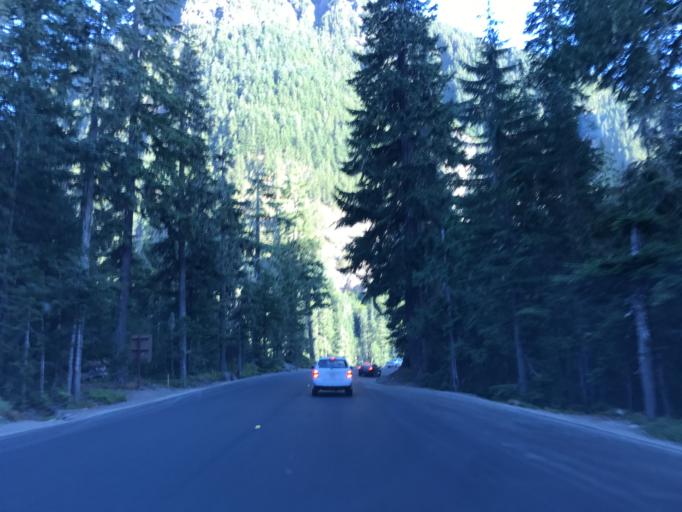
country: US
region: Washington
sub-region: Pierce County
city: Buckley
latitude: 46.7678
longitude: -121.7913
